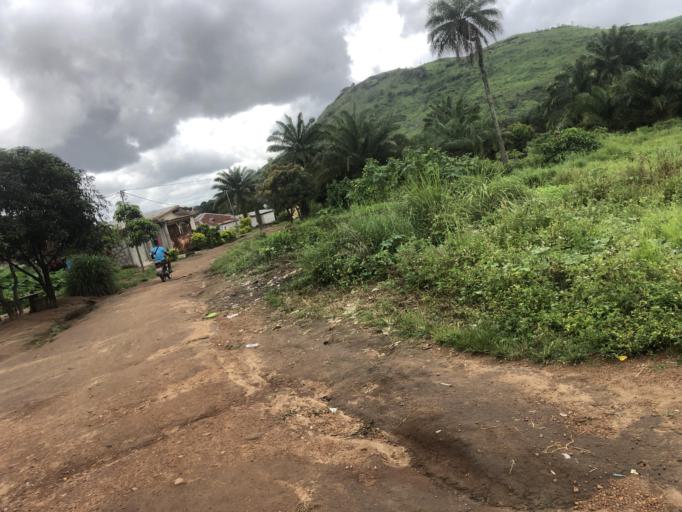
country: SL
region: Northern Province
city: Makeni
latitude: 8.9104
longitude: -12.0417
